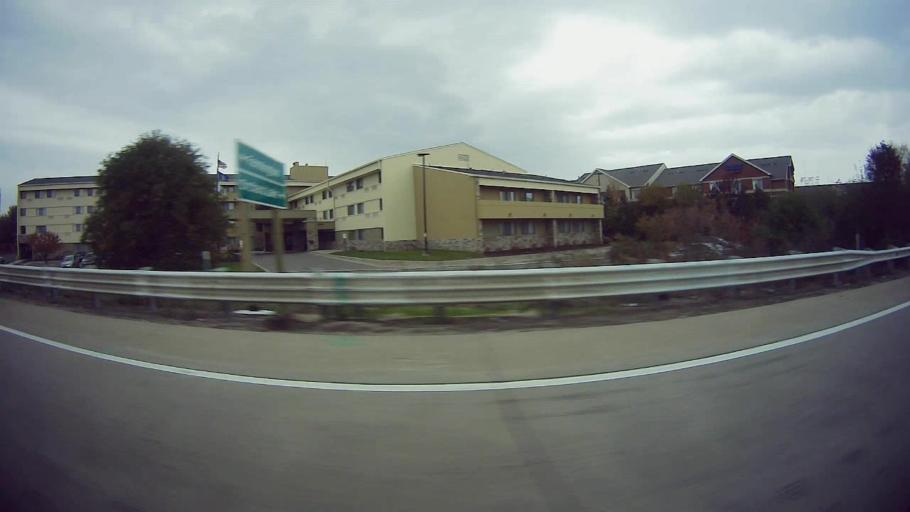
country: US
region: Michigan
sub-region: Oakland County
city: Farmington Hills
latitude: 42.4974
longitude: -83.3563
